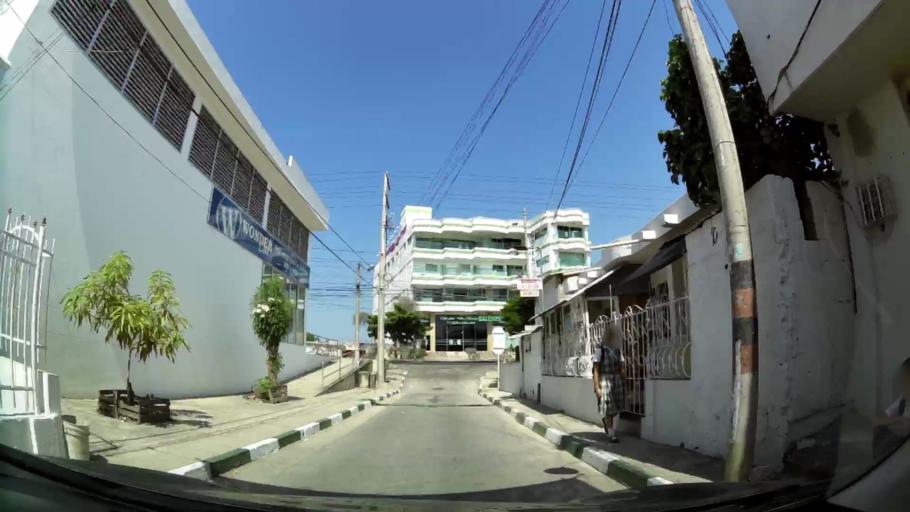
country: CO
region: Bolivar
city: Cartagena
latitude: 10.3825
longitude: -75.4669
